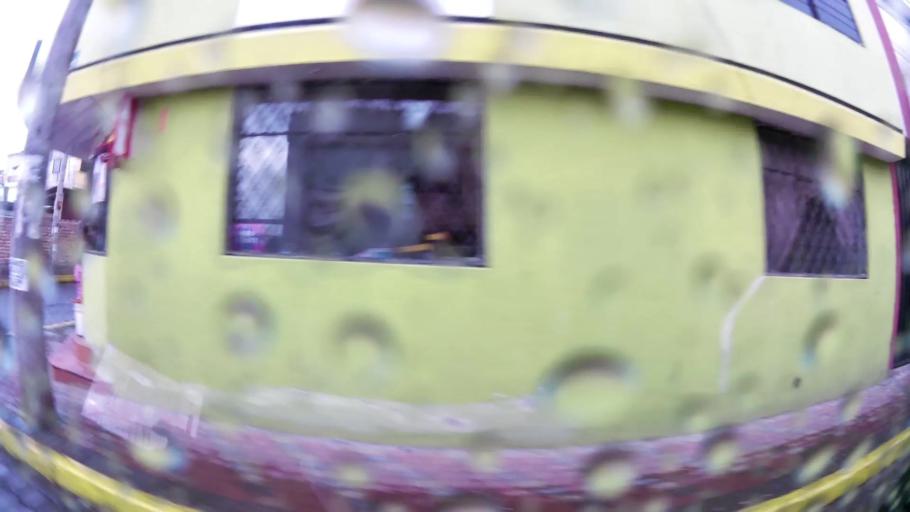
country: EC
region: Pichincha
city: Quito
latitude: -0.3208
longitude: -78.5518
